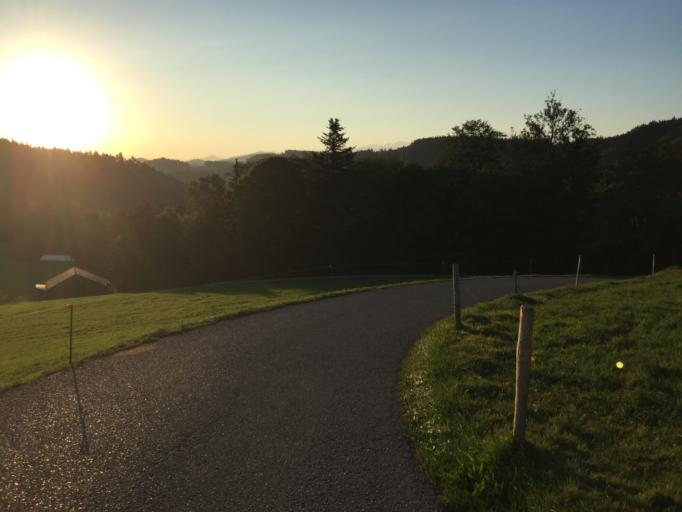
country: CH
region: Saint Gallen
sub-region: Wahlkreis Wil
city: Oberuzwil
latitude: 47.4111
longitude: 9.1383
